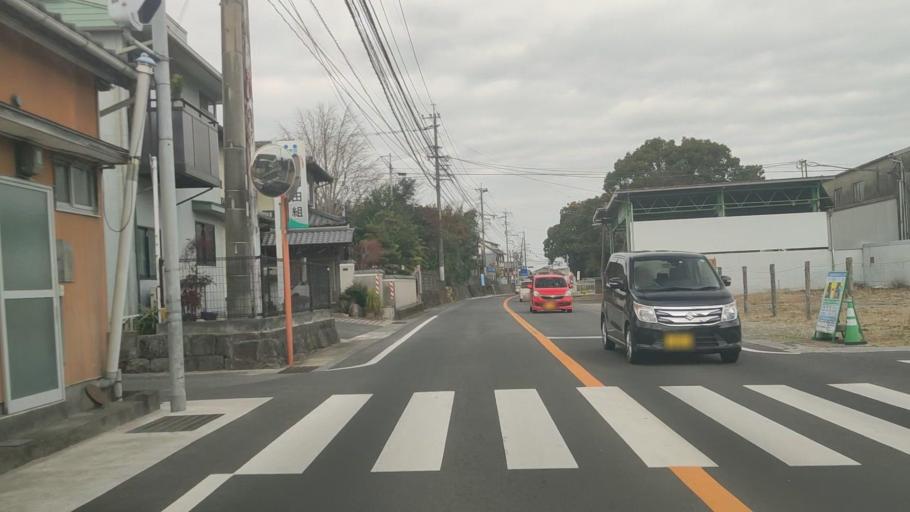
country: JP
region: Nagasaki
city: Shimabara
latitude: 32.8176
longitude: 130.3549
